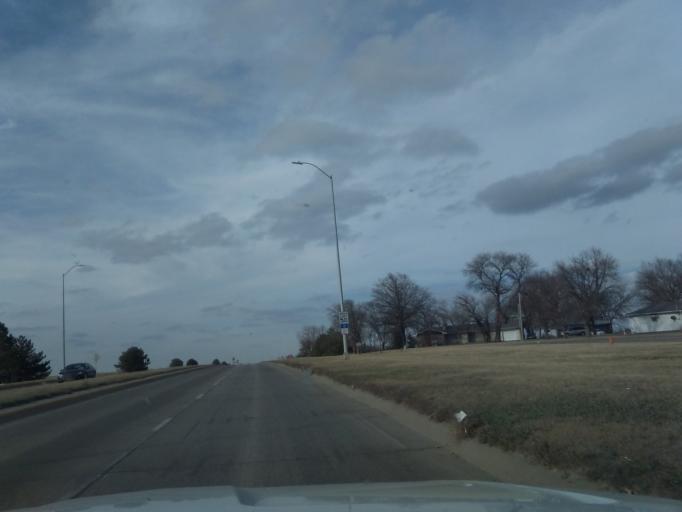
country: US
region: Nebraska
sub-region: Gage County
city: Beatrice
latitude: 40.2924
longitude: -96.7466
